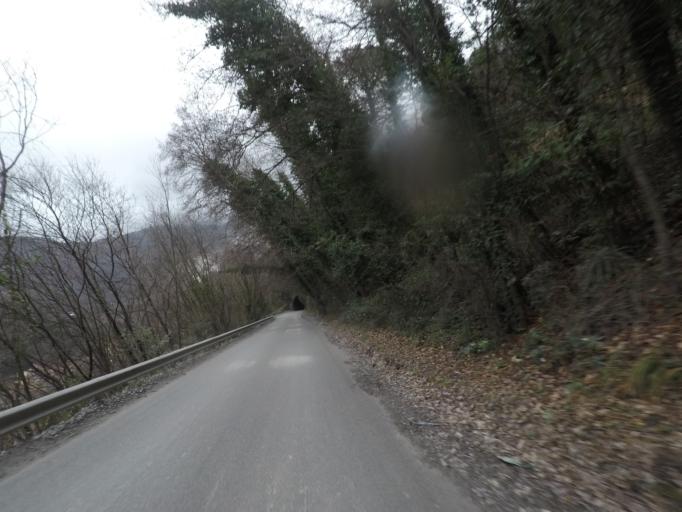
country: IT
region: Tuscany
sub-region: Provincia di Massa-Carrara
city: Carrara
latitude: 44.0890
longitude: 10.1058
